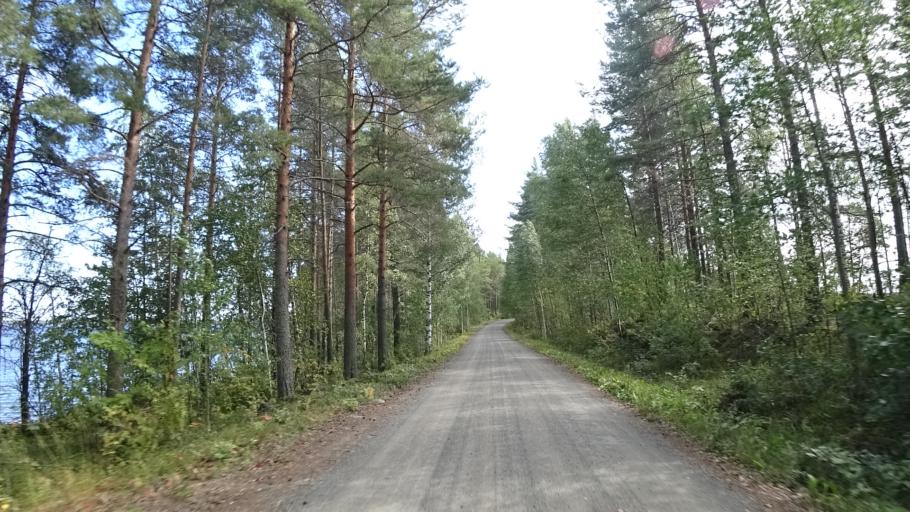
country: FI
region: North Karelia
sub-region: Keski-Karjala
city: Raeaekkylae
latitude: 62.3952
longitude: 29.7663
